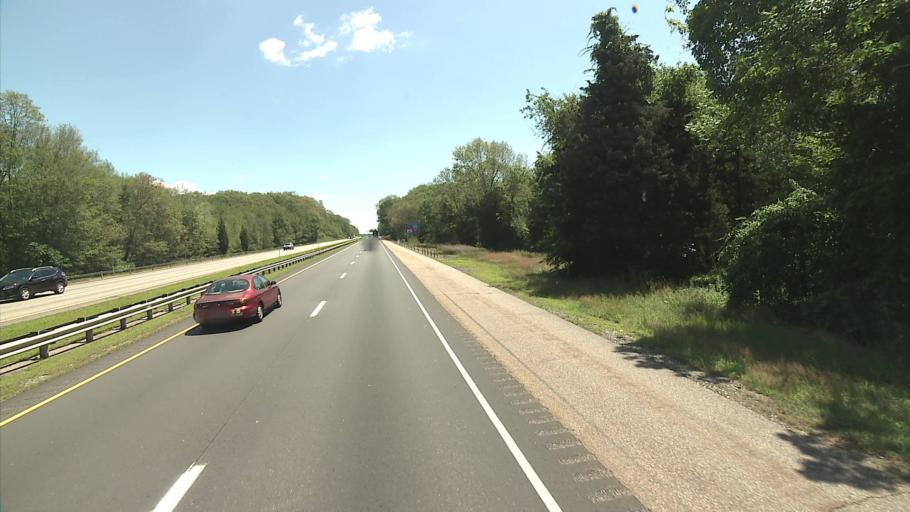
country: US
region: Connecticut
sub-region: New London County
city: Lisbon
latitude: 41.5898
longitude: -72.0089
